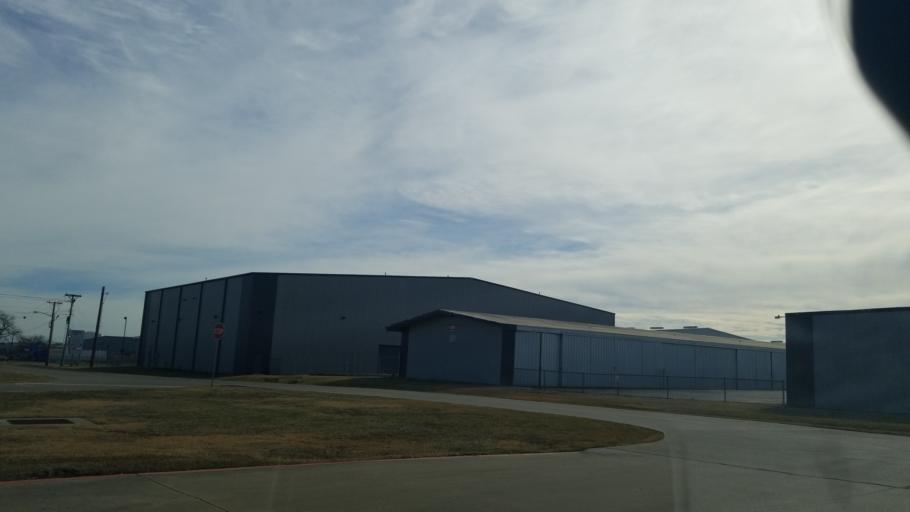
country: US
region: Texas
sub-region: Denton County
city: Denton
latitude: 33.2021
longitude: -97.1942
